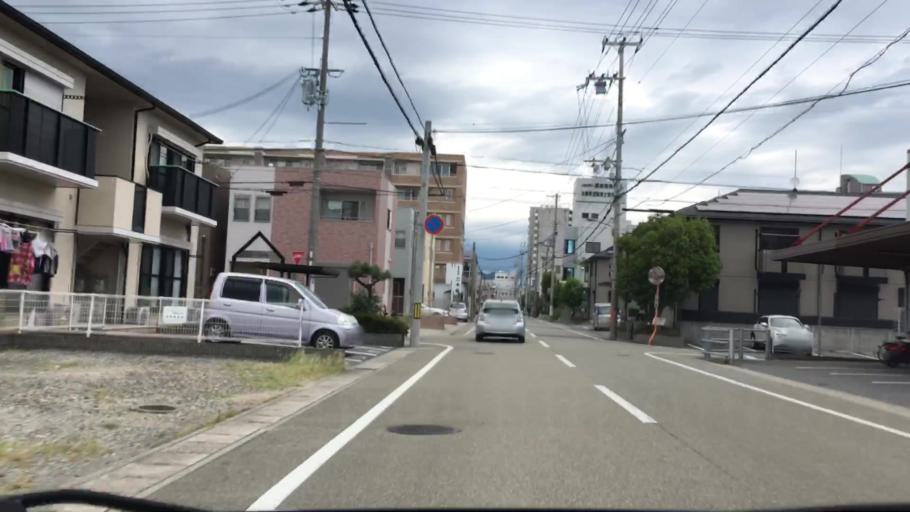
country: JP
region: Hyogo
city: Himeji
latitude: 34.8185
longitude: 134.6928
